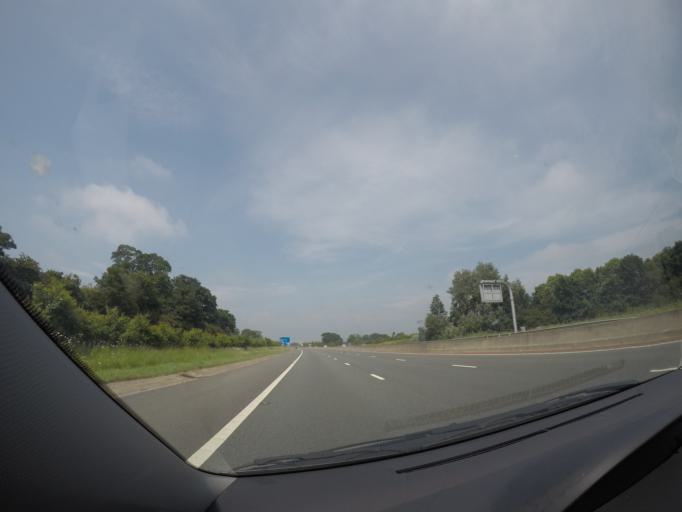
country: GB
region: England
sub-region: North Yorkshire
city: Bedale
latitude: 54.2917
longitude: -1.5502
